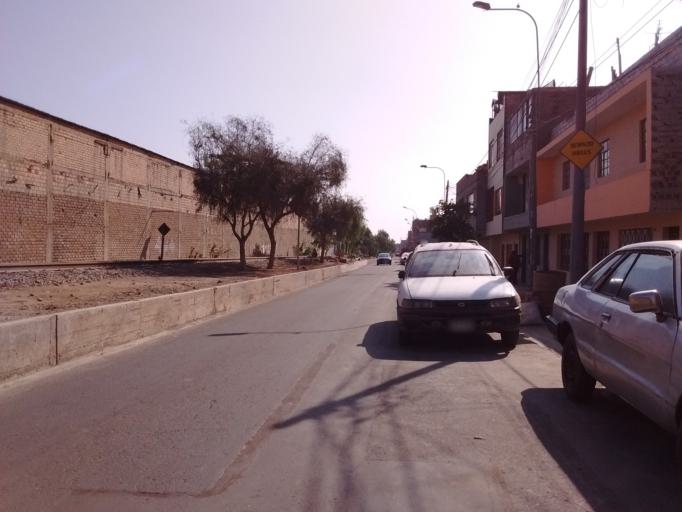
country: PE
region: Callao
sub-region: Callao
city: Callao
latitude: -12.0387
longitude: -77.0793
